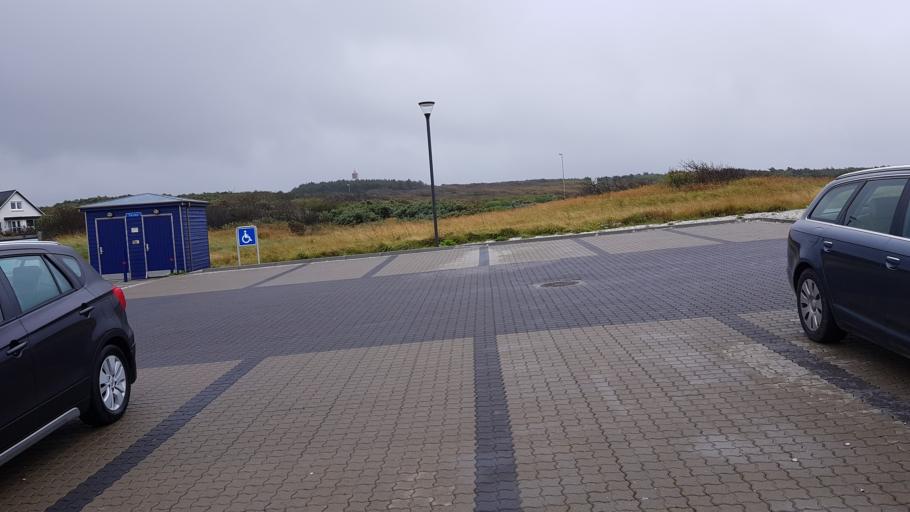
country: DK
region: North Denmark
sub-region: Thisted Kommune
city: Hanstholm
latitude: 57.1170
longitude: 8.5955
